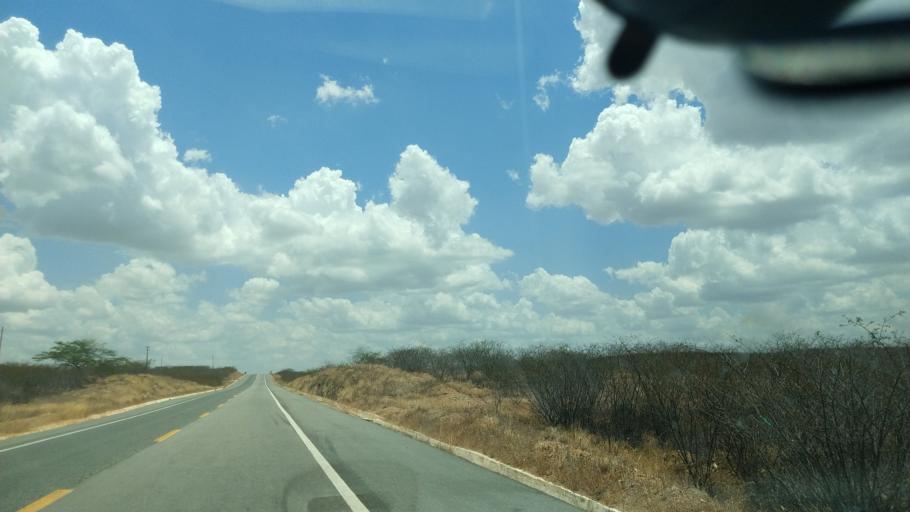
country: BR
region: Rio Grande do Norte
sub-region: Currais Novos
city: Currais Novos
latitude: -6.2466
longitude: -36.4696
